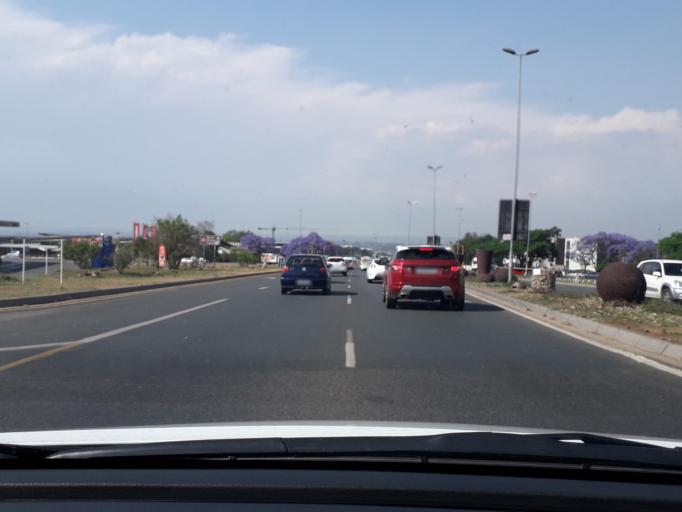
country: ZA
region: Gauteng
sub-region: West Rand District Municipality
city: Muldersdriseloop
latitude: -26.0450
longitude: 27.9542
